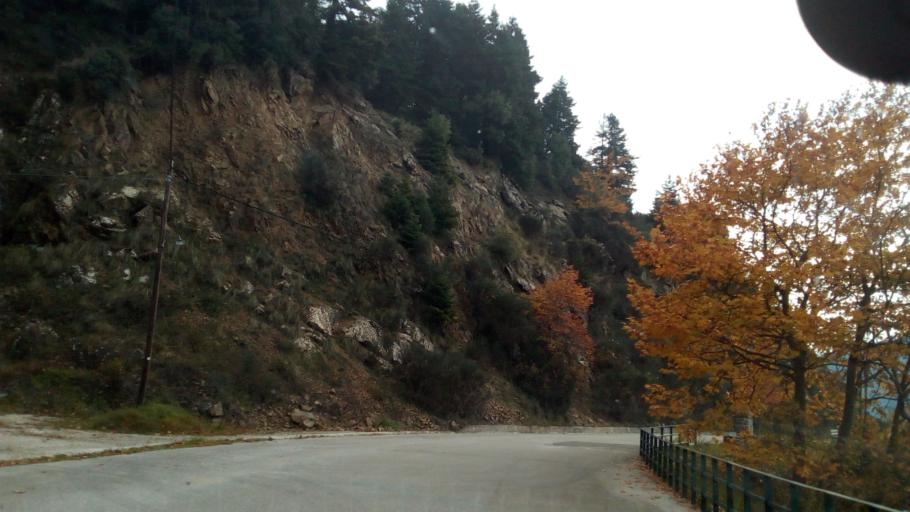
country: GR
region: West Greece
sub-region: Nomos Aitolias kai Akarnanias
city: Thermo
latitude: 38.6869
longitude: 21.8686
